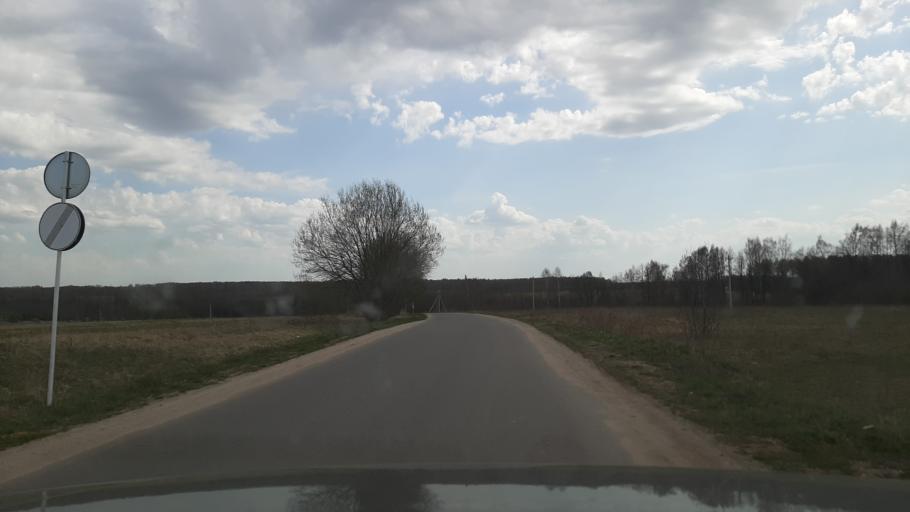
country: RU
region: Ivanovo
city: Furmanov
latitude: 57.3193
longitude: 41.1639
